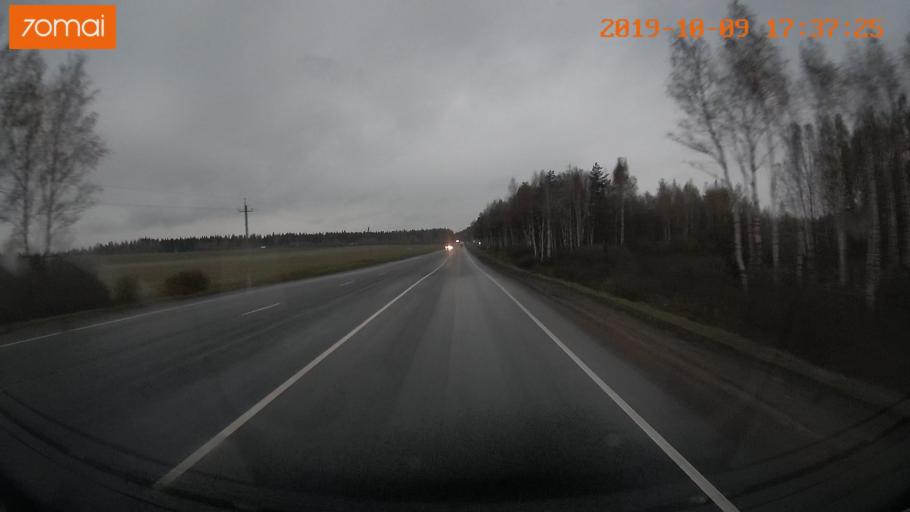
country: RU
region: Ivanovo
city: Bogorodskoye
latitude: 57.0709
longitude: 40.9797
